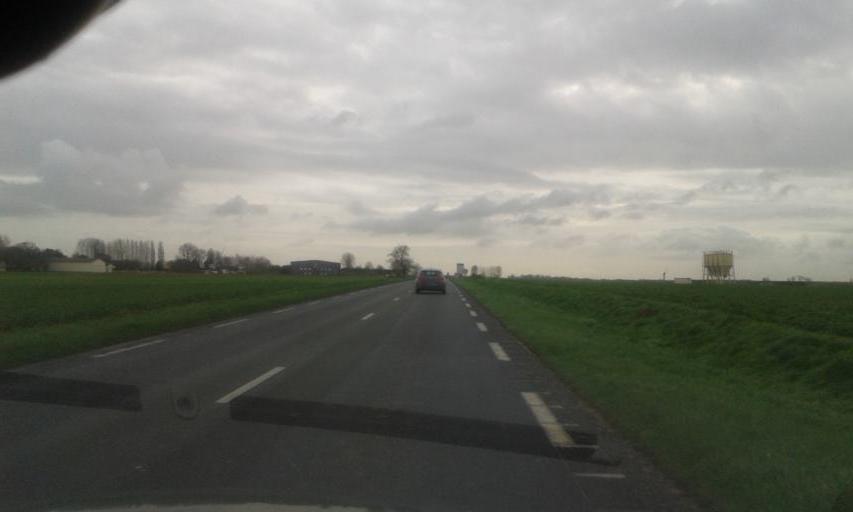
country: FR
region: Haute-Normandie
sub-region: Departement de la Seine-Maritime
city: Montmain
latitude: 49.3856
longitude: 1.2473
